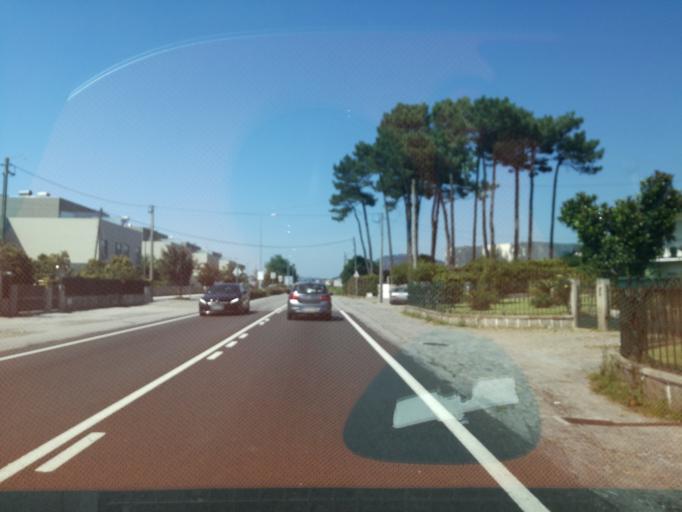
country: PT
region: Braga
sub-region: Esposende
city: Esposende
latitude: 41.5467
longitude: -8.7824
